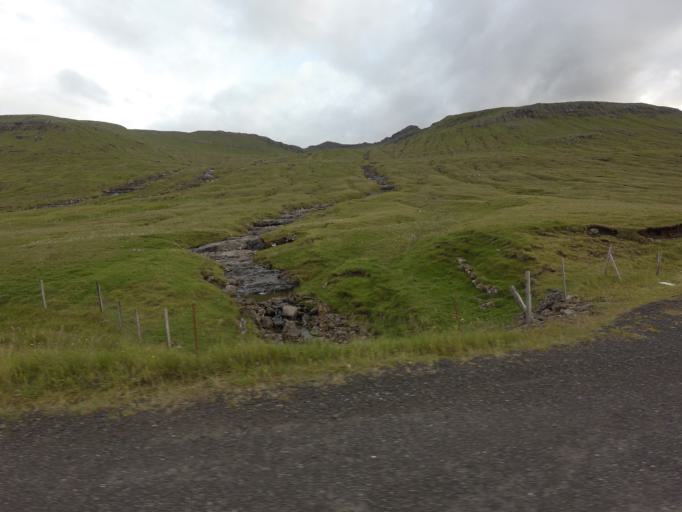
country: FO
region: Streymoy
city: Kollafjordhur
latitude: 62.1829
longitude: -7.0085
